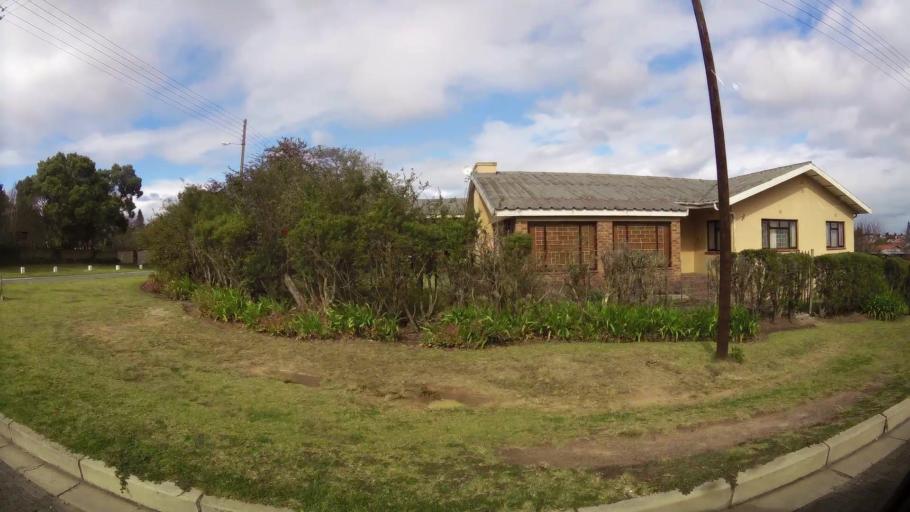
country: ZA
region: Western Cape
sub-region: Eden District Municipality
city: George
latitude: -34.0018
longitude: 22.4450
